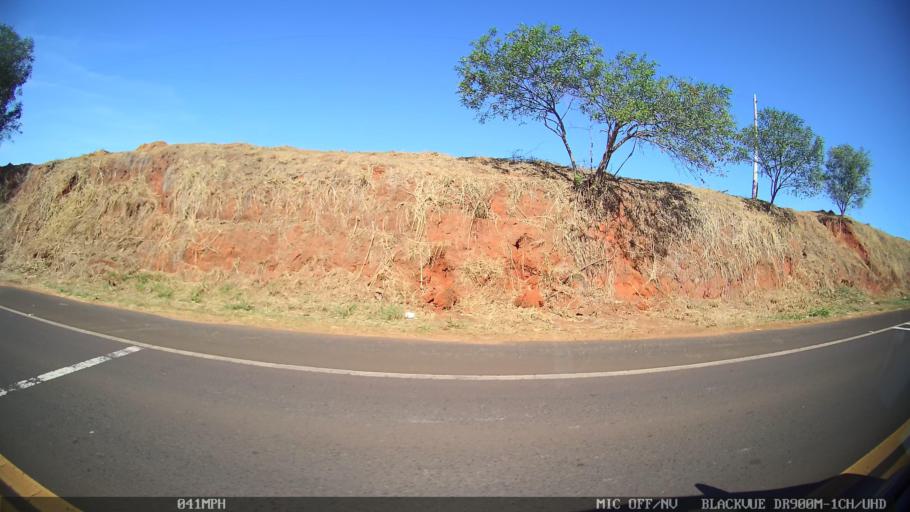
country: BR
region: Sao Paulo
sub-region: Olimpia
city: Olimpia
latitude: -20.7288
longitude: -48.8676
